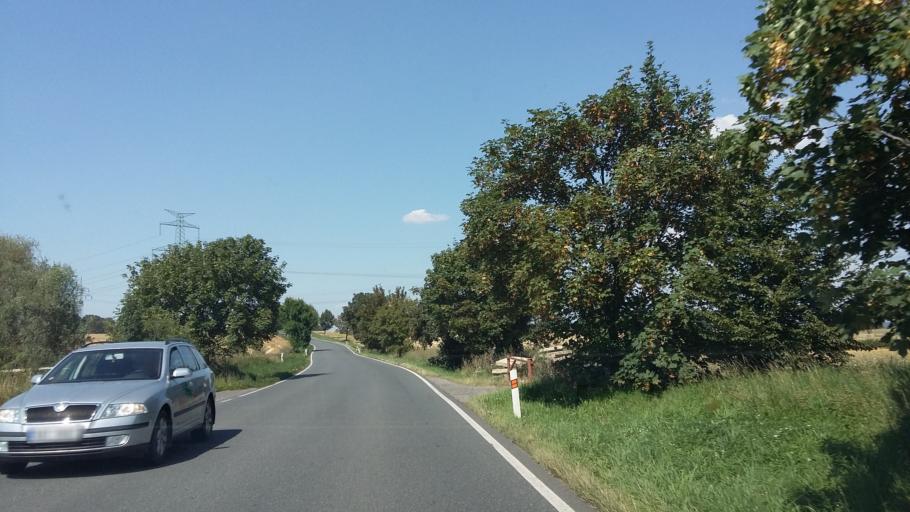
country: CZ
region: Central Bohemia
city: Zelenec
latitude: 50.1497
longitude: 14.6884
